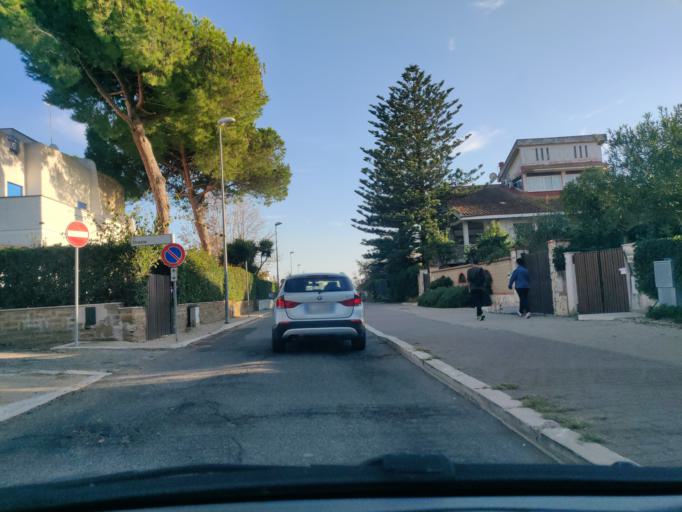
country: IT
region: Latium
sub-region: Citta metropolitana di Roma Capitale
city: Santa Marinella
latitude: 42.0319
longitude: 11.8343
